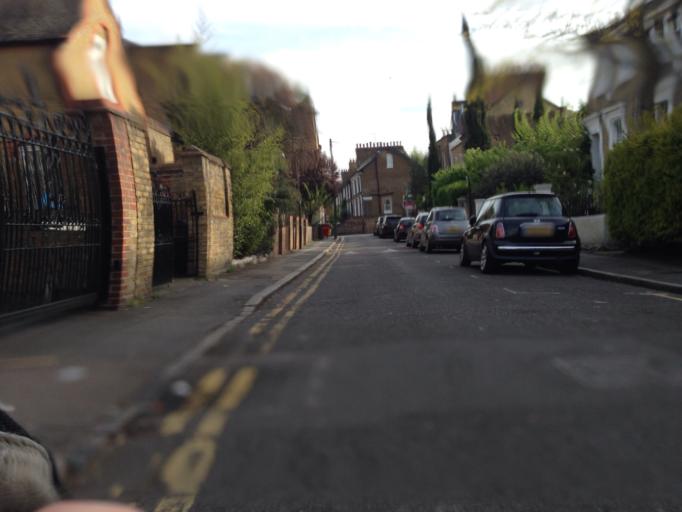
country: GB
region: England
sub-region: Greater London
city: Brixton Hill
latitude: 51.4743
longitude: -0.1286
